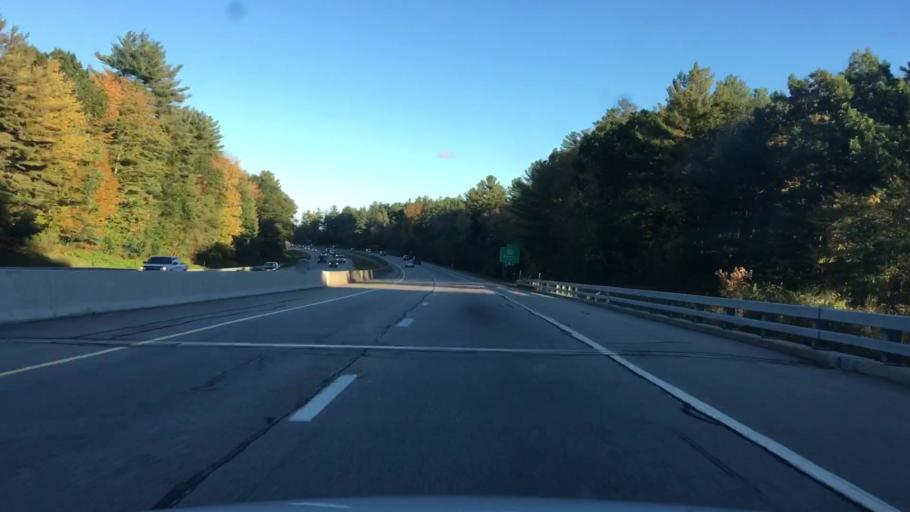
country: US
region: New Hampshire
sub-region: Rockingham County
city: Exeter
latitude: 43.0085
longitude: -71.0027
